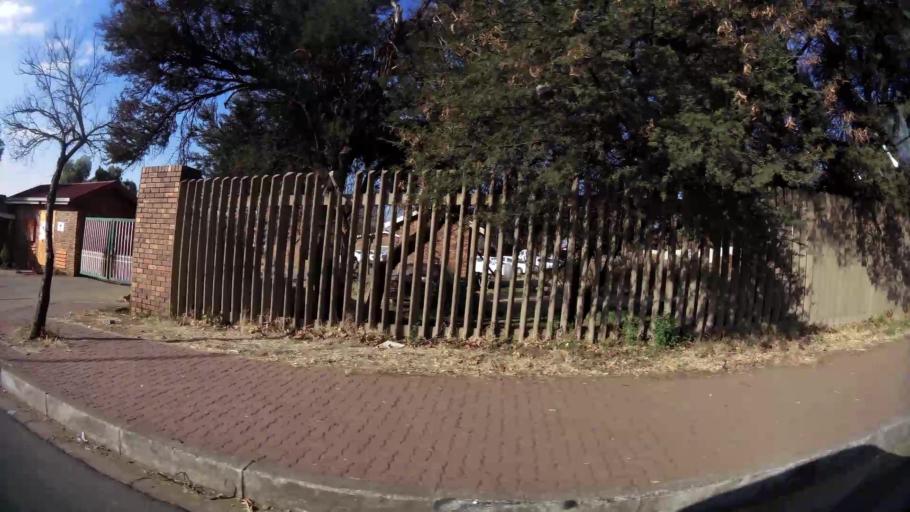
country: ZA
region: Gauteng
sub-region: City of Johannesburg Metropolitan Municipality
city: Soweto
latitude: -26.2607
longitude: 27.9150
